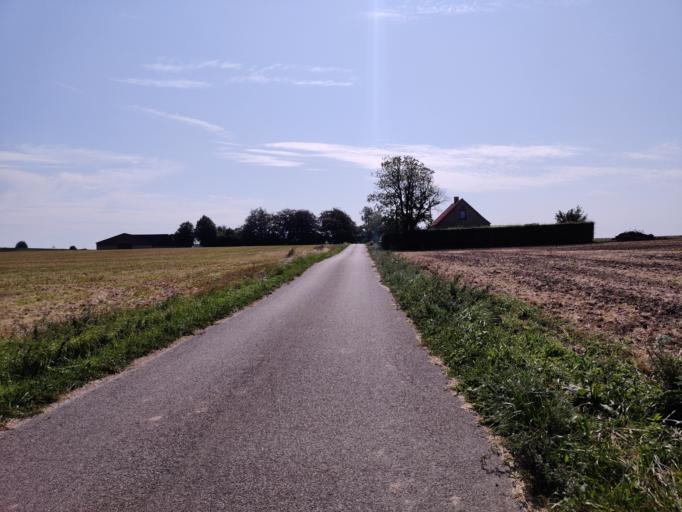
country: DK
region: Zealand
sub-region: Guldborgsund Kommune
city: Nykobing Falster
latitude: 54.6795
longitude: 11.8908
